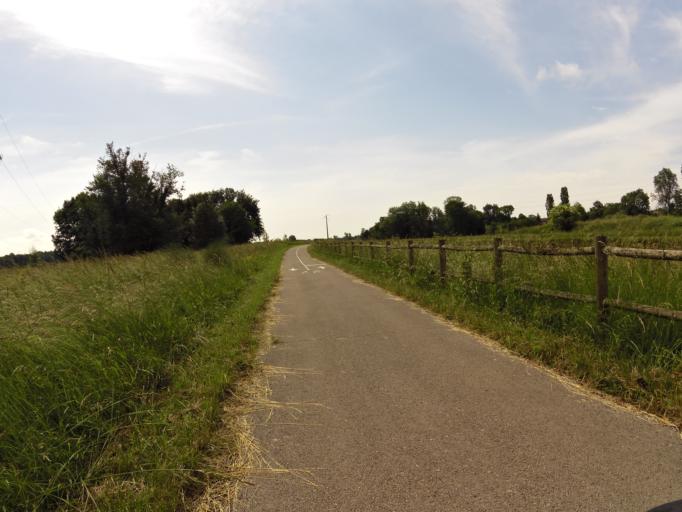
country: FR
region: Champagne-Ardenne
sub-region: Departement de l'Aube
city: Lusigny-sur-Barse
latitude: 48.2642
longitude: 4.2670
